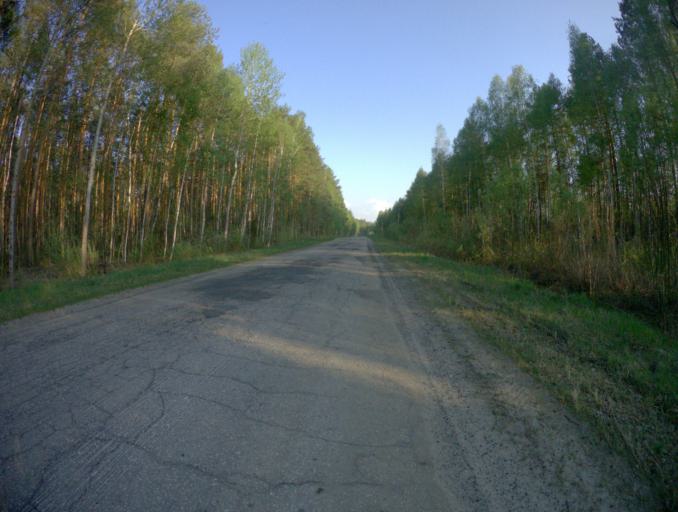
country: RU
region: Vladimir
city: Vyazniki
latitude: 56.3476
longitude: 42.1376
